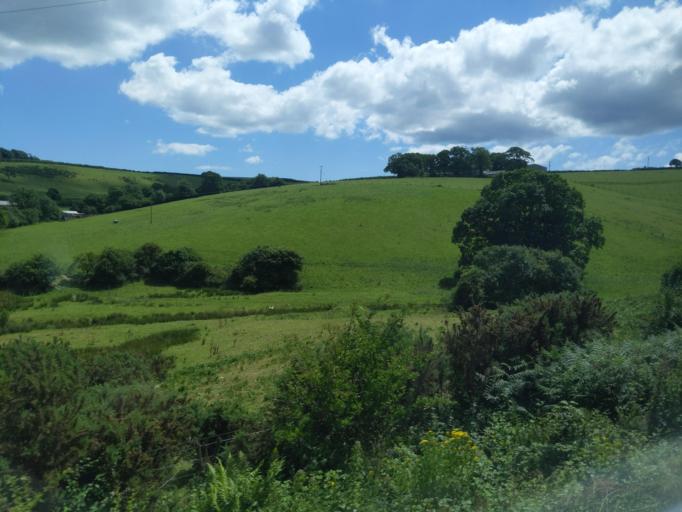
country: GB
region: England
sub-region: Cornwall
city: Lostwithiel
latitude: 50.3865
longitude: -4.6705
